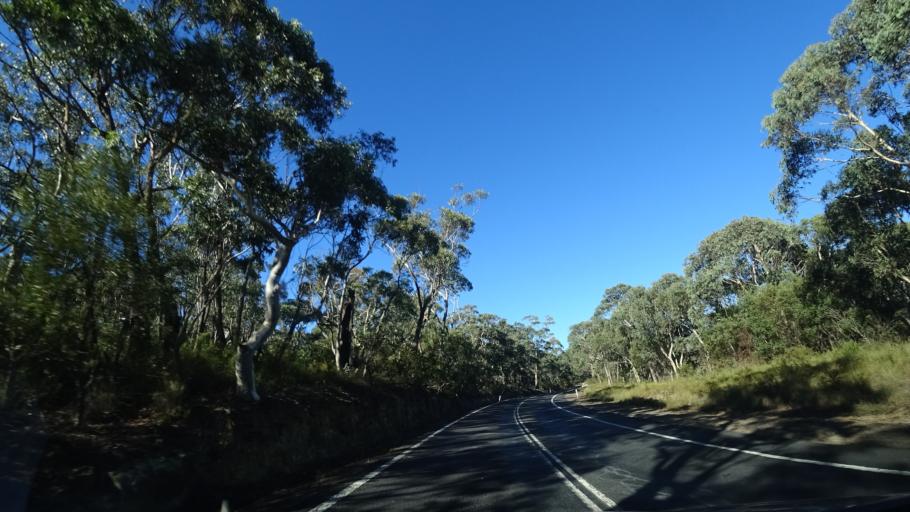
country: AU
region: New South Wales
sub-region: Blue Mountains Municipality
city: Blackheath
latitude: -33.5500
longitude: 150.3830
